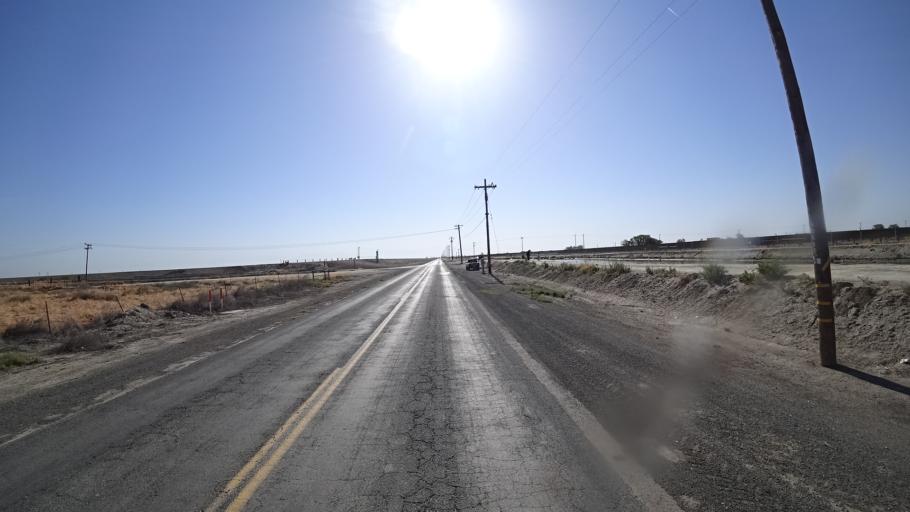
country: US
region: California
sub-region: Kings County
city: Corcoran
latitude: 36.1379
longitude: -119.5660
